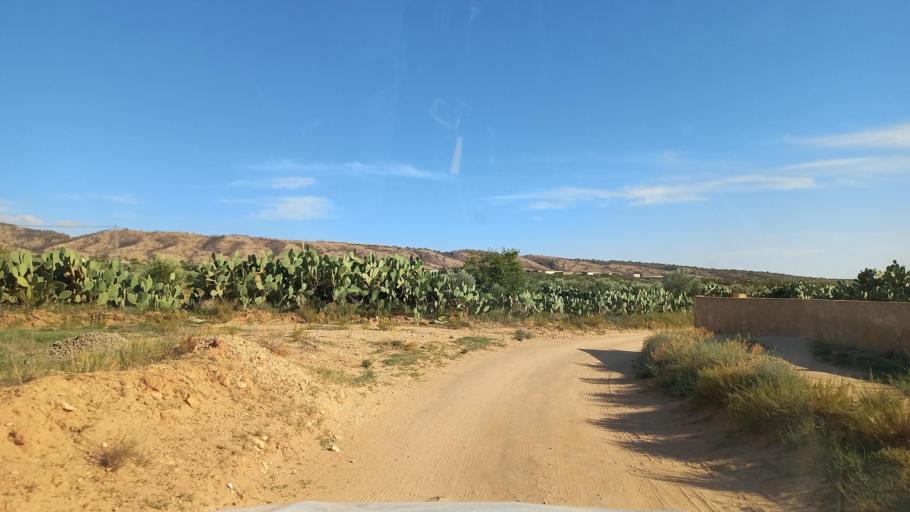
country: TN
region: Al Qasrayn
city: Sbiba
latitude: 35.3347
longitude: 9.1250
